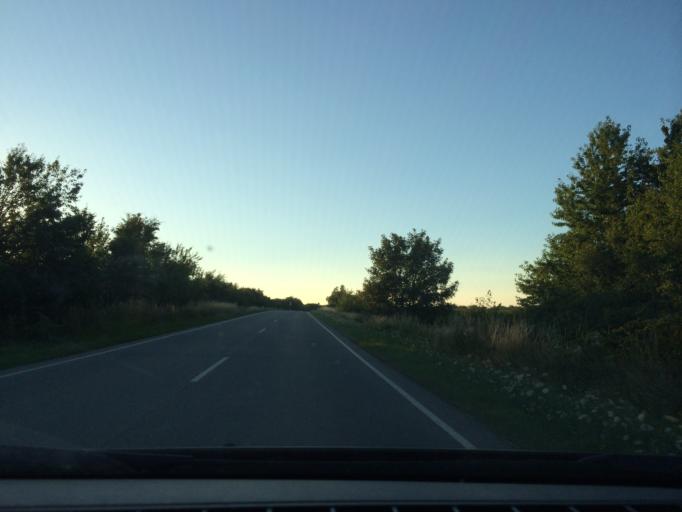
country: DK
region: Zealand
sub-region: Vordingborg Kommune
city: Praesto
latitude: 55.0507
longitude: 12.0915
